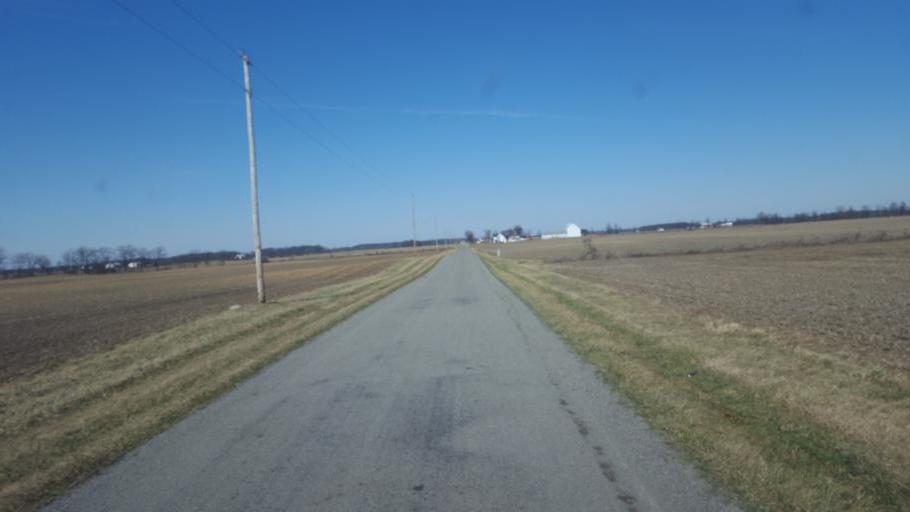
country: US
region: Ohio
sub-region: Union County
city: Richwood
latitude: 40.5251
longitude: -83.4542
